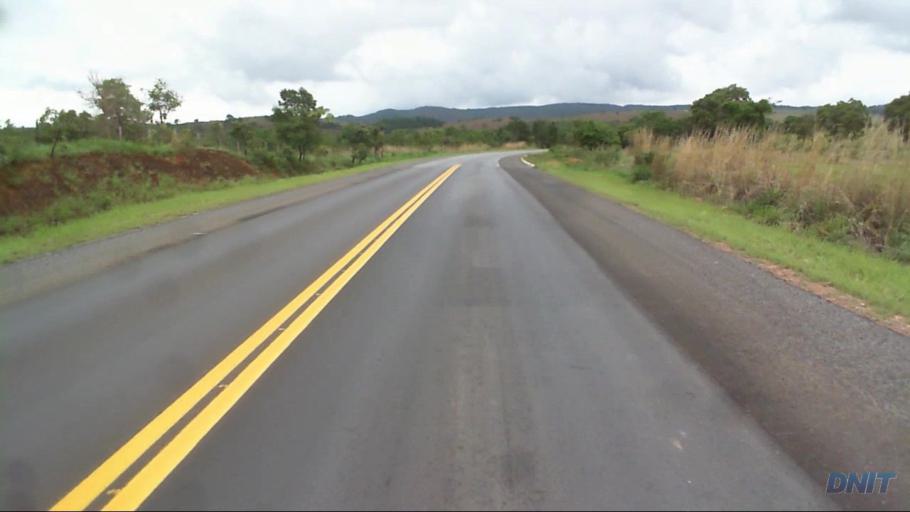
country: BR
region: Goias
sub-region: Padre Bernardo
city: Padre Bernardo
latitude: -15.2171
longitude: -48.5136
